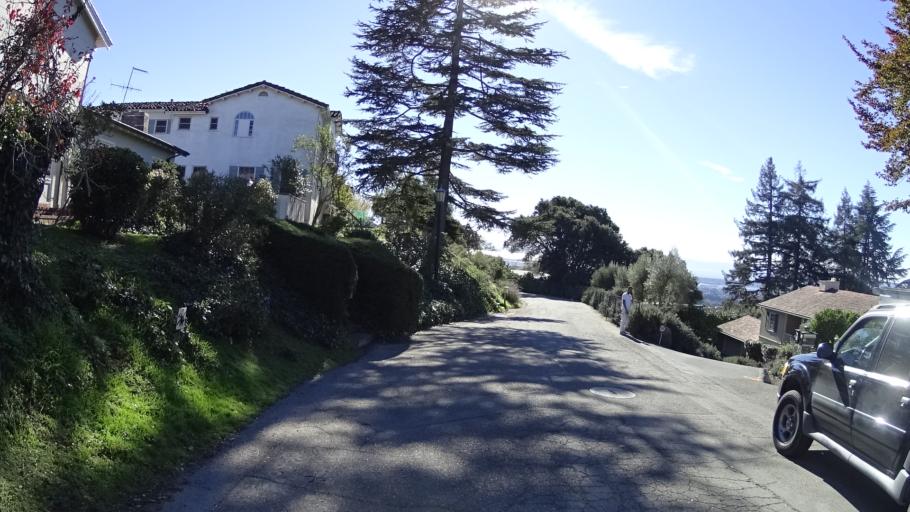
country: US
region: California
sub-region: Alameda County
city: Piedmont
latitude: 37.8283
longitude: -122.2211
